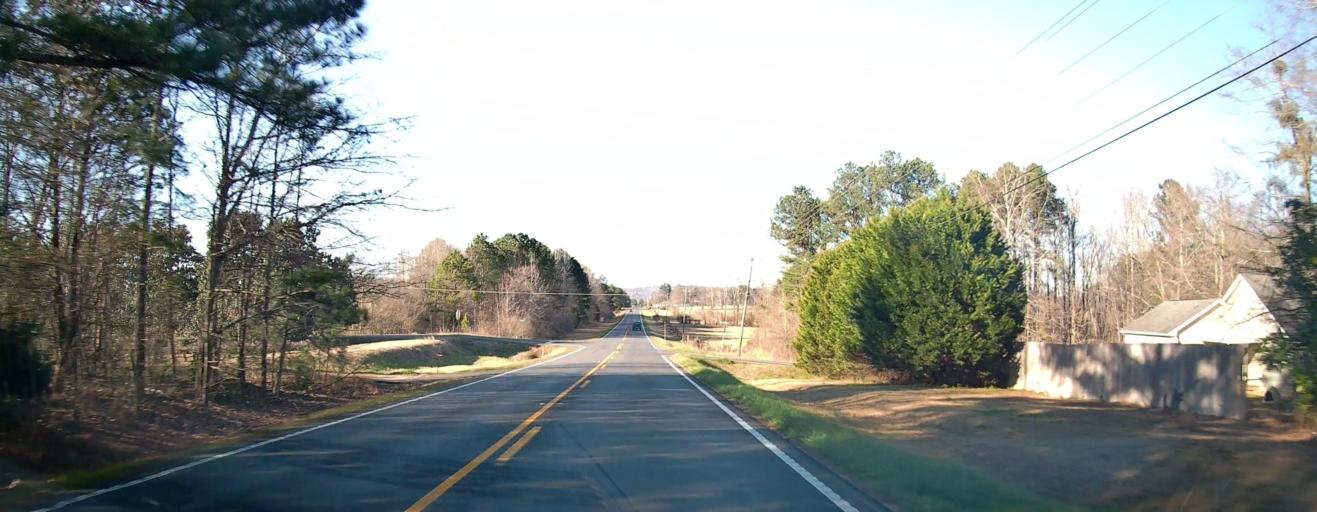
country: US
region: Georgia
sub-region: Talbot County
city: Sardis
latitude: 32.8123
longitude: -84.6970
